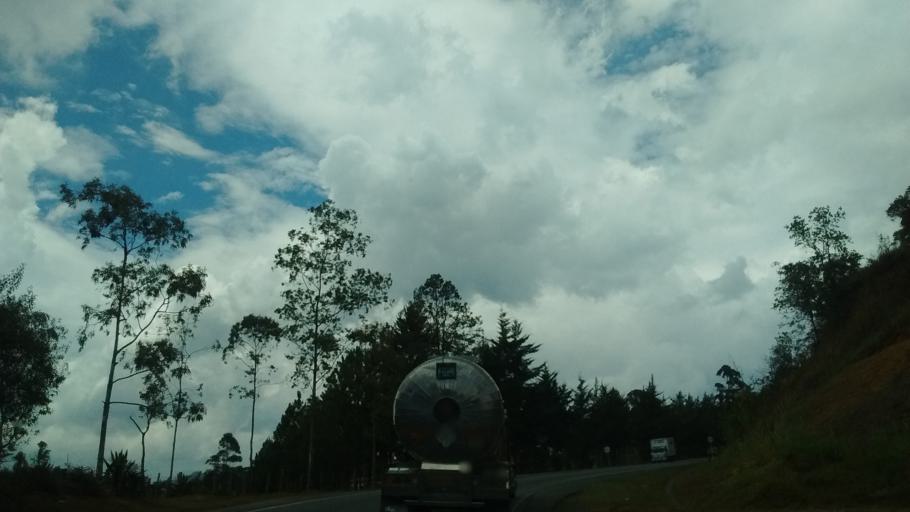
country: CO
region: Cauca
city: Rosas
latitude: 2.3346
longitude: -76.6912
